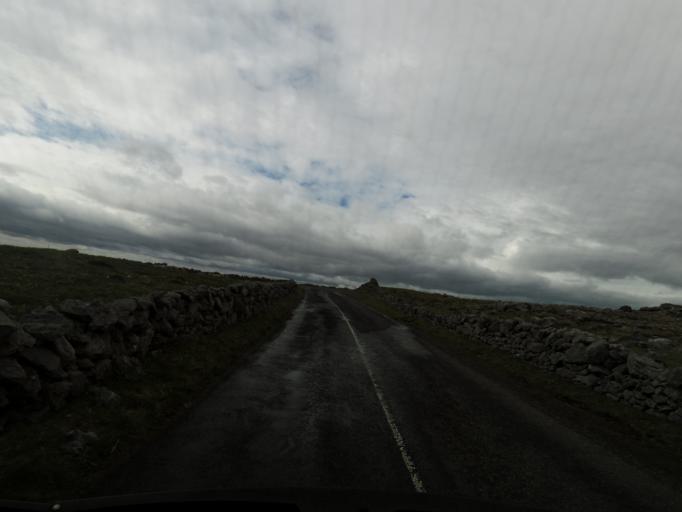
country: IE
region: Connaught
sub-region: County Galway
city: Bearna
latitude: 53.0597
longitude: -9.3619
